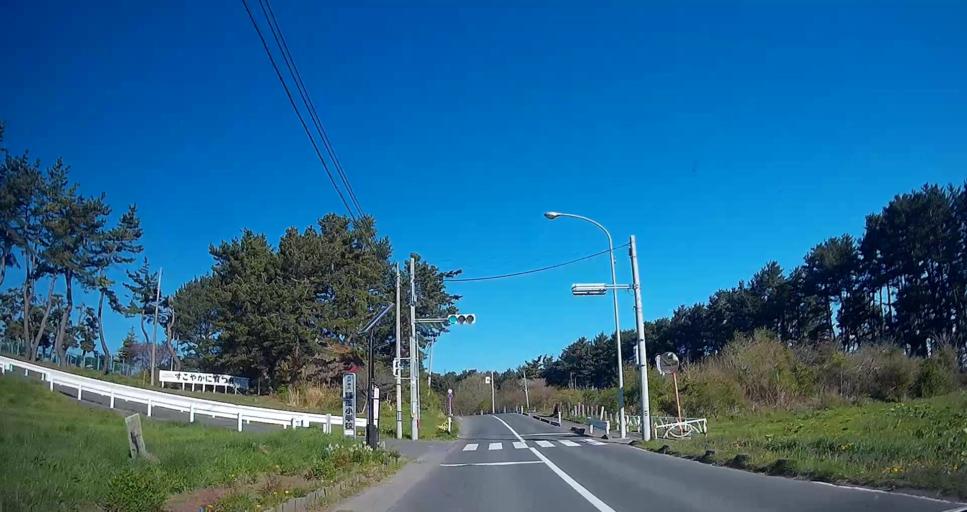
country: JP
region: Aomori
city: Hachinohe
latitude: 40.5141
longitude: 141.6048
